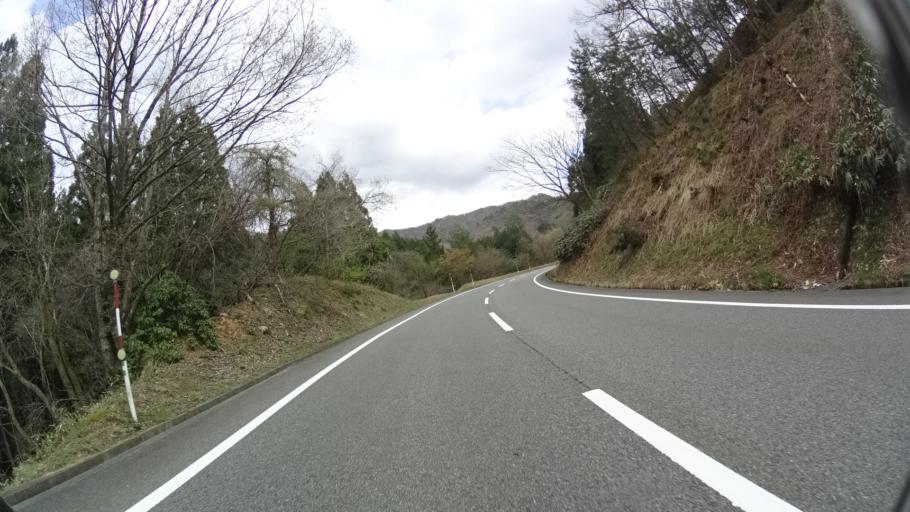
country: JP
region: Hyogo
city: Toyooka
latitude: 35.5079
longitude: 134.8962
